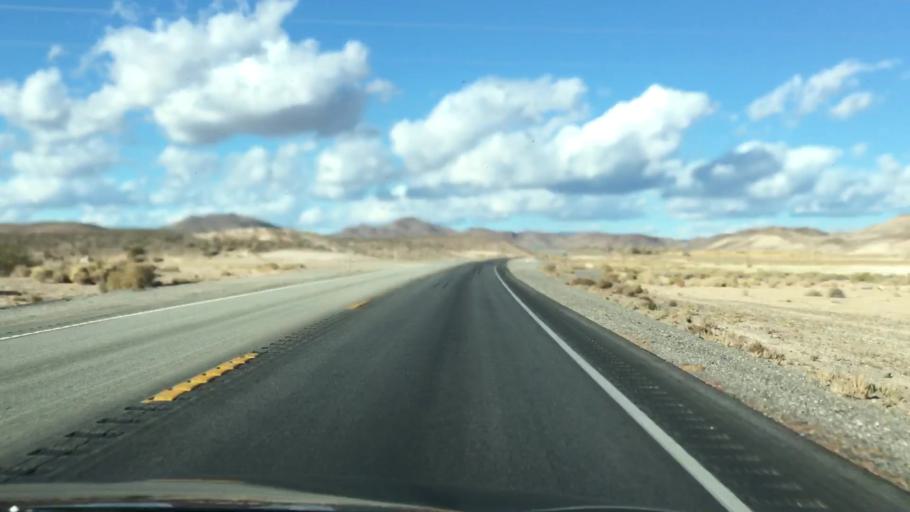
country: US
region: Nevada
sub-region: Nye County
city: Beatty
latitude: 36.9887
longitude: -116.7252
